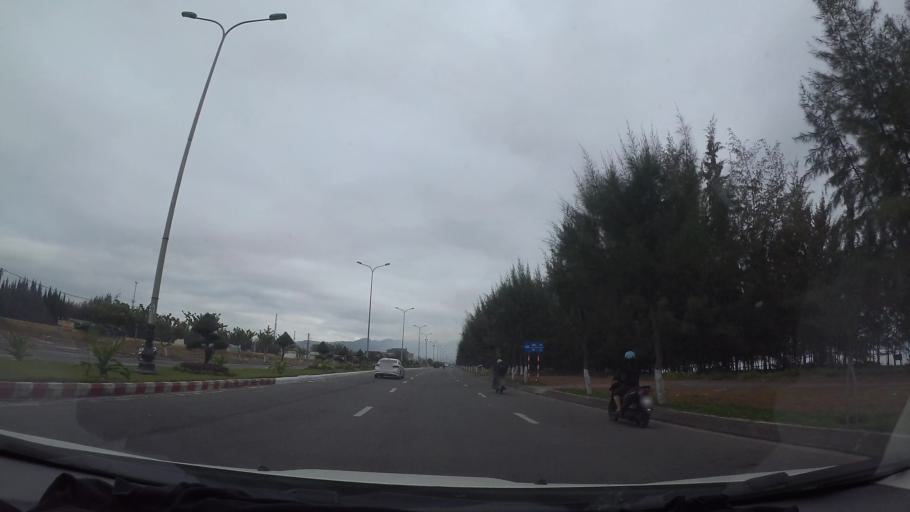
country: VN
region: Da Nang
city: Lien Chieu
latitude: 16.0980
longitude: 108.1430
